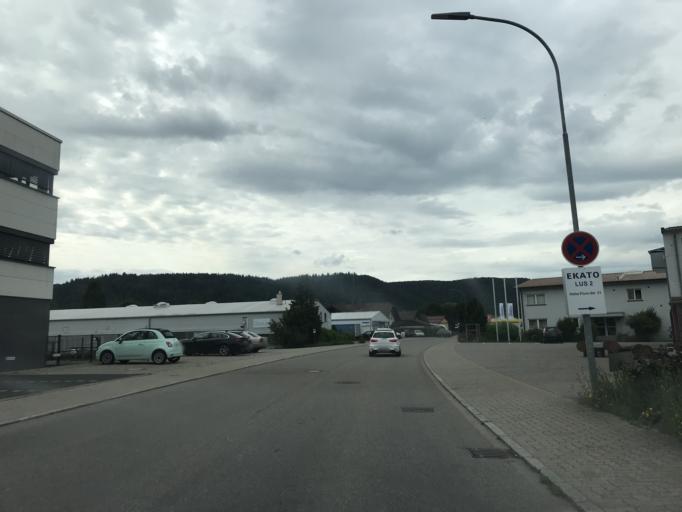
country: DE
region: Baden-Wuerttemberg
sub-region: Freiburg Region
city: Schopfheim
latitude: 47.6434
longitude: 7.8037
